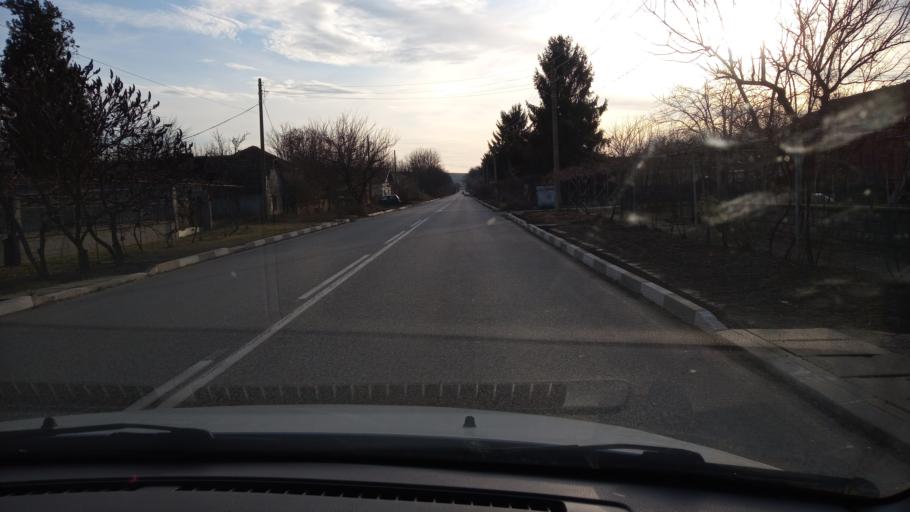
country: BG
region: Pleven
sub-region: Obshtina Pleven
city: Slavyanovo
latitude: 43.5589
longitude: 24.8679
